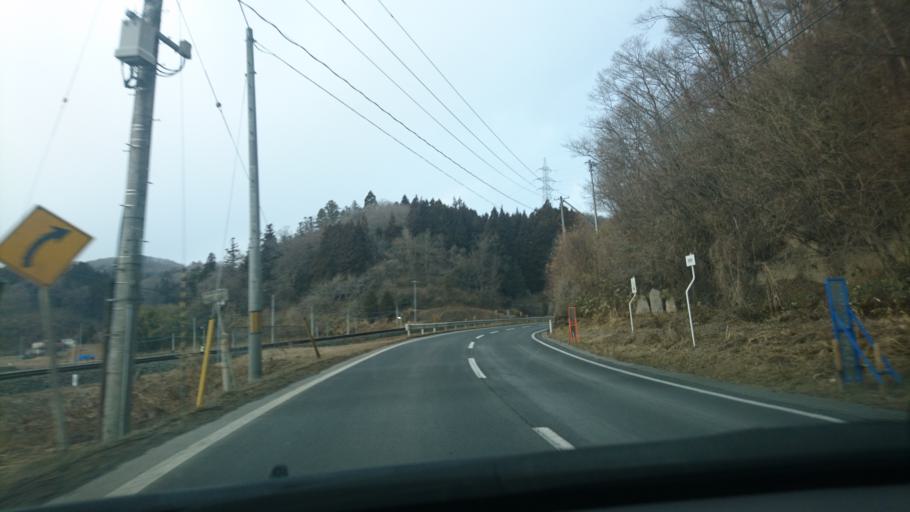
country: JP
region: Iwate
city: Ichinoseki
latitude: 38.9538
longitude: 141.3343
